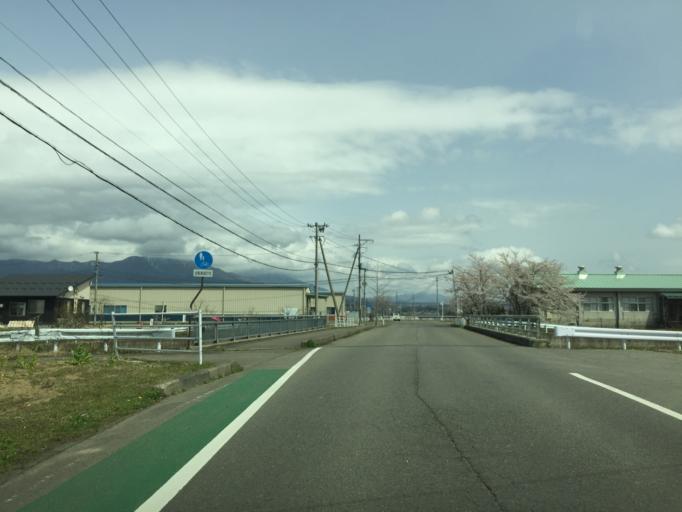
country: JP
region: Fukushima
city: Kitakata
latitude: 37.5640
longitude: 139.8849
